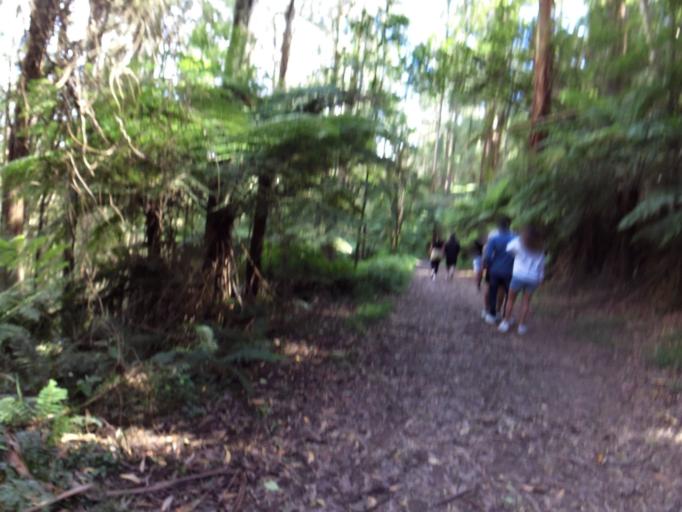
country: AU
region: Victoria
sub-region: Yarra Ranges
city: Belgrave
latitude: -37.8913
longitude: 145.3516
